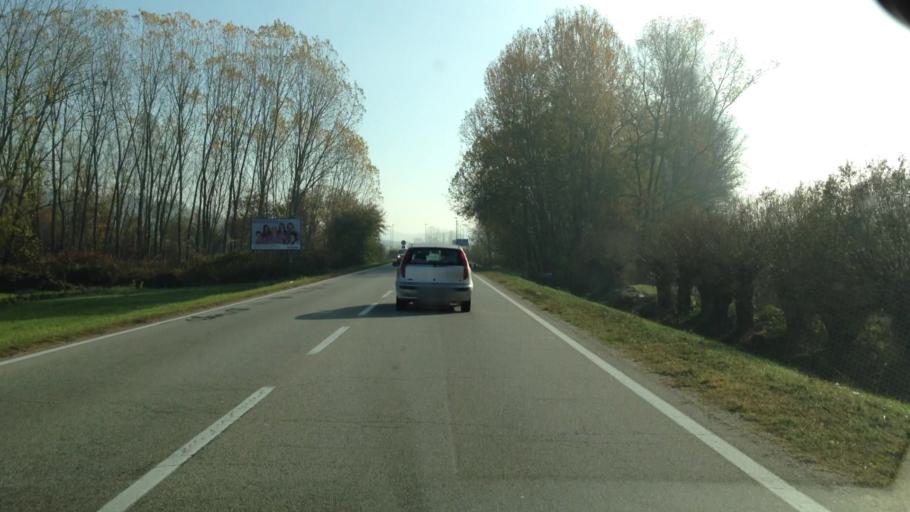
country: IT
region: Piedmont
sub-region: Provincia di Asti
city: Vigliano d'Asti
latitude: 44.8240
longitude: 8.2204
